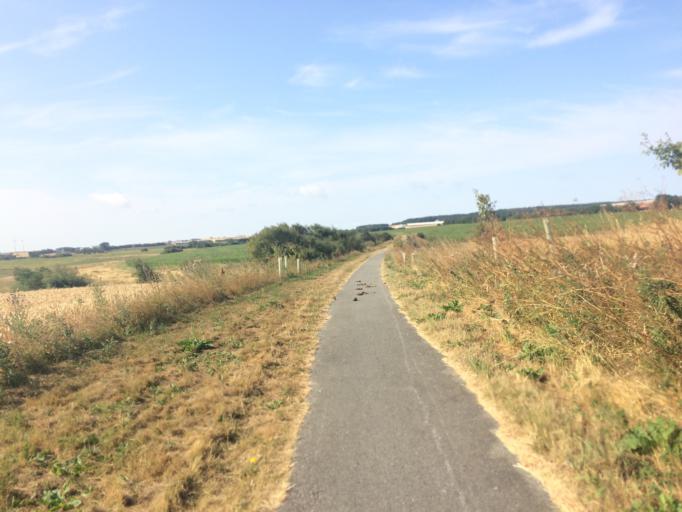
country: DK
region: Central Jutland
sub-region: Holstebro Kommune
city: Vinderup
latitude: 56.6241
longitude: 8.7805
